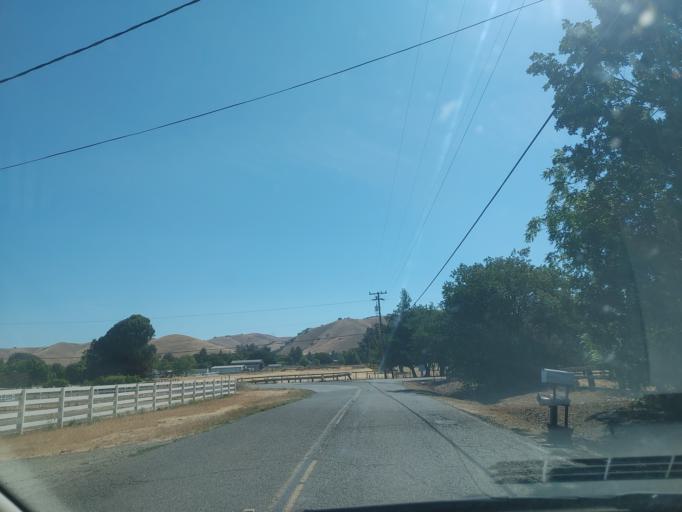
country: US
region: California
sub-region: San Benito County
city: Hollister
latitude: 36.9063
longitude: -121.3517
